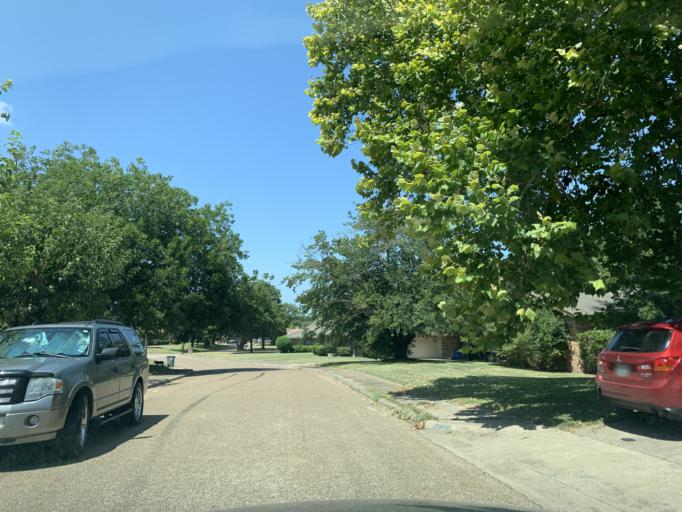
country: US
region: Texas
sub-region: Dallas County
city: Cockrell Hill
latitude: 32.6804
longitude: -96.8077
